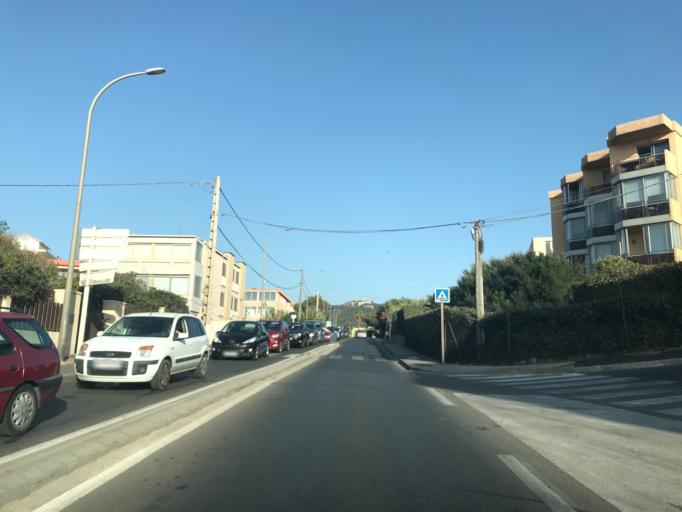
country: FR
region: Provence-Alpes-Cote d'Azur
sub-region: Departement du Var
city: Sanary-sur-Mer
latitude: 43.1081
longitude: 5.8147
